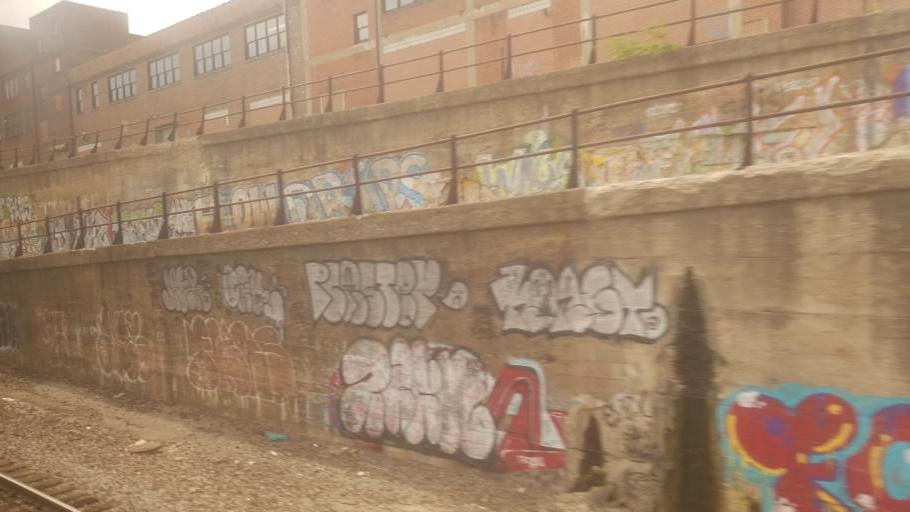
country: US
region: Missouri
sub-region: Jackson County
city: Kansas City
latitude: 39.0884
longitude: -94.5671
